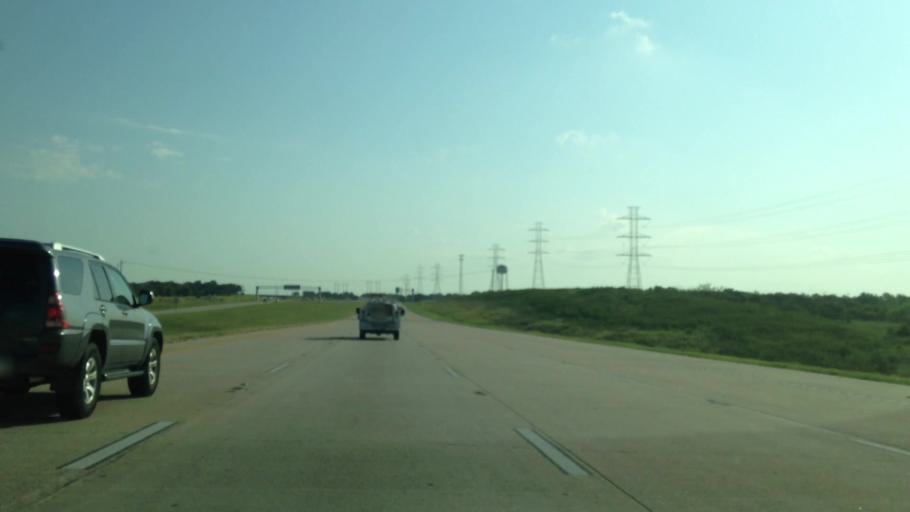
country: US
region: Texas
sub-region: Travis County
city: Hornsby Bend
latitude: 30.2760
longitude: -97.5870
